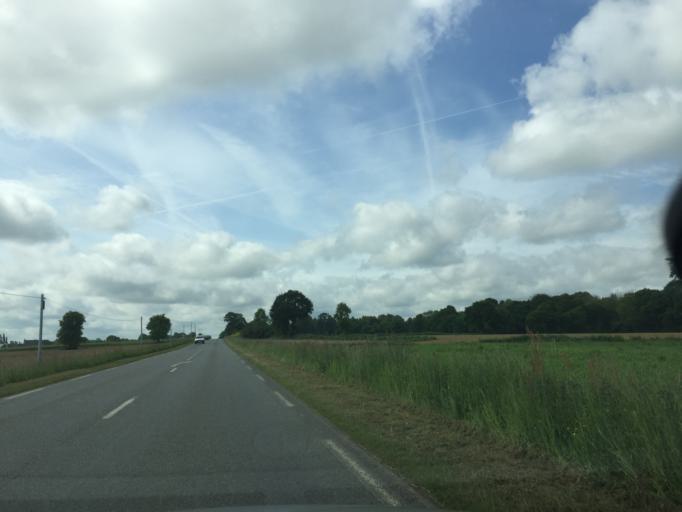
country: FR
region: Brittany
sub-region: Departement des Cotes-d'Armor
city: Crehen
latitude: 48.5593
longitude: -2.1912
